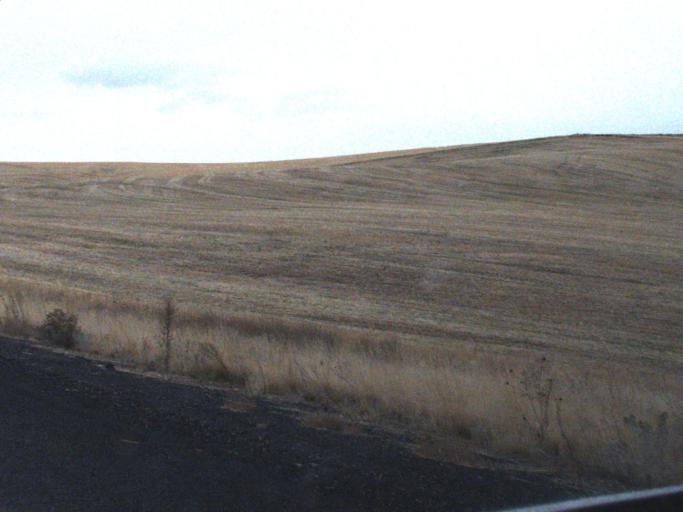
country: US
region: Washington
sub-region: Garfield County
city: Pomeroy
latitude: 46.8116
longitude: -117.8172
